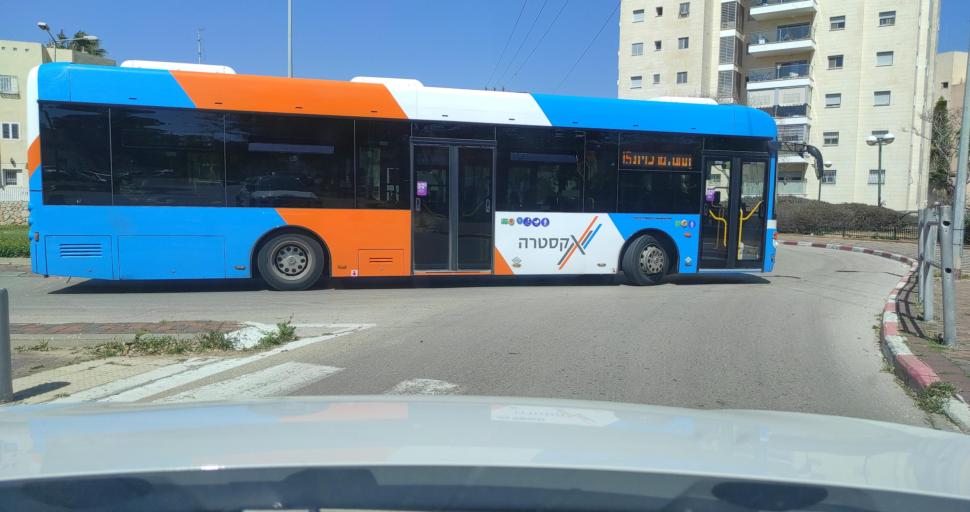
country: IL
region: Central District
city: Nordiyya
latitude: 32.3064
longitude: 34.8829
